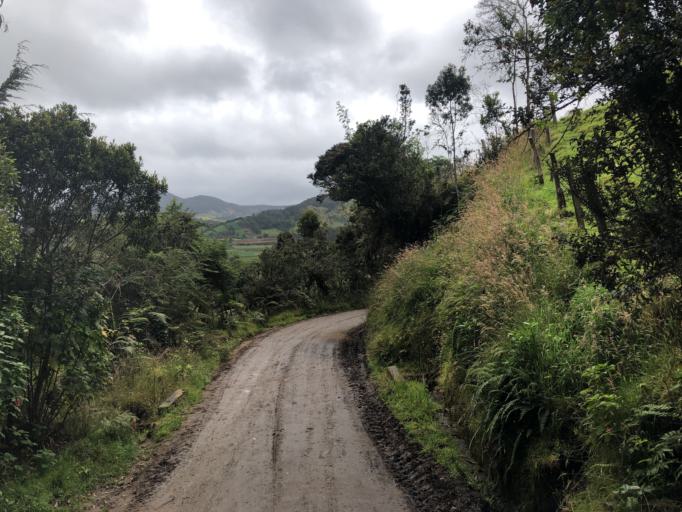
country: CO
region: Cauca
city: Totoro
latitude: 2.4985
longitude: -76.2863
